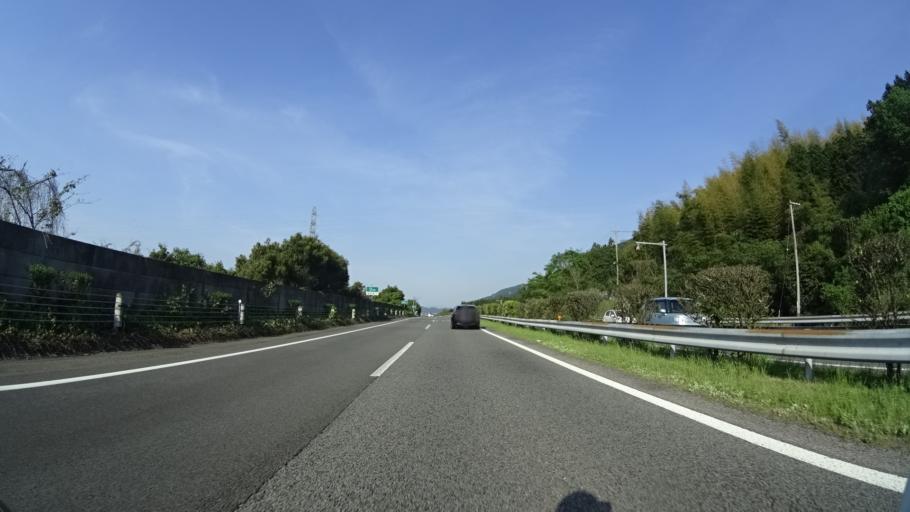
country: JP
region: Ehime
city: Niihama
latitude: 33.9155
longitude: 133.2825
